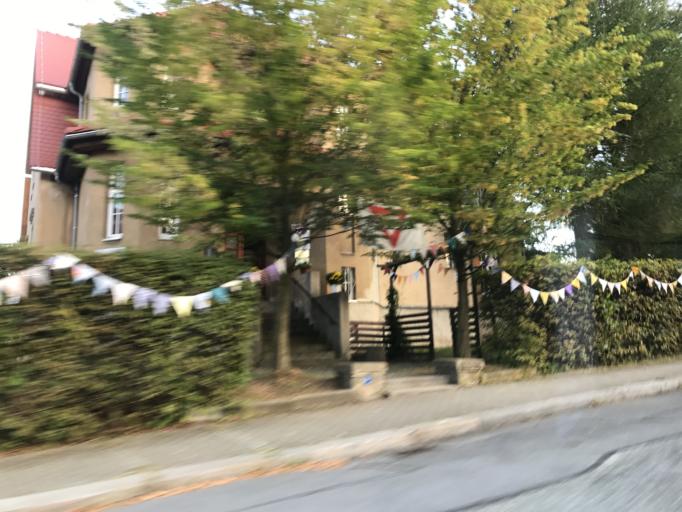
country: DE
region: Saxony
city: Lobau
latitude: 51.0927
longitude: 14.6645
